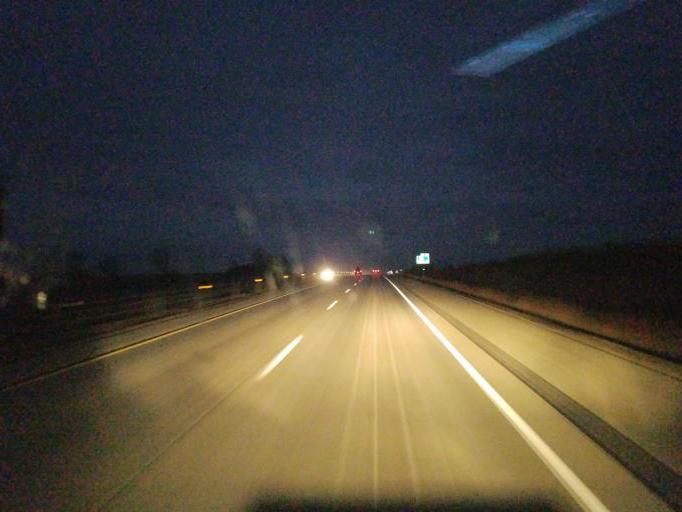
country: US
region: Iowa
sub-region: Guthrie County
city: Guthrie Center
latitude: 41.4961
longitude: -94.5279
